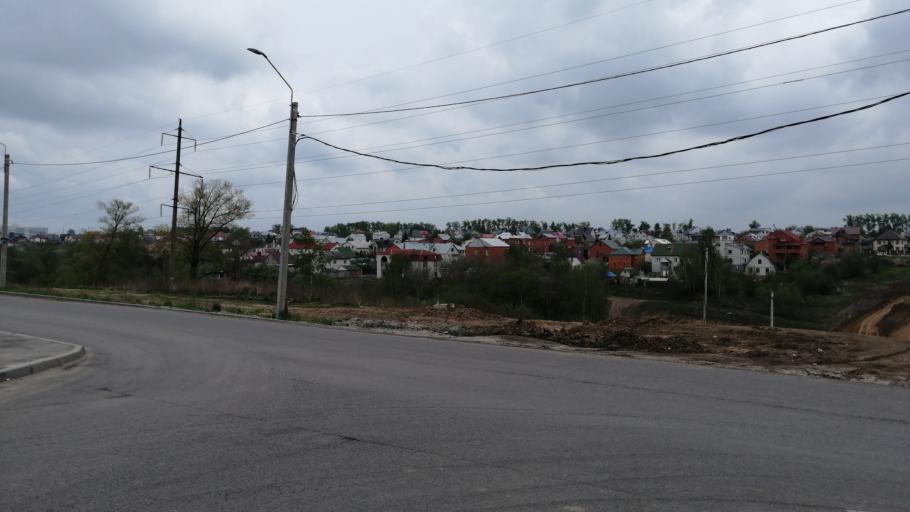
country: RU
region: Kursk
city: Kursk
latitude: 51.7182
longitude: 36.1191
